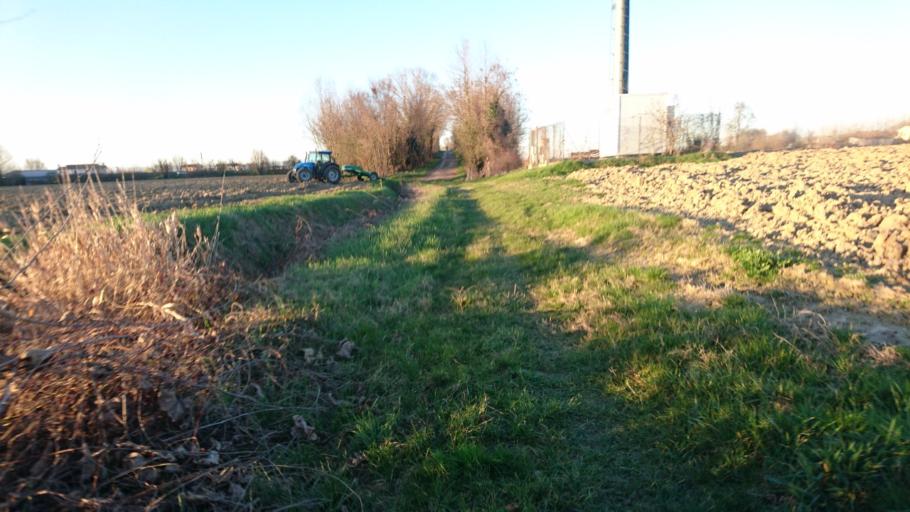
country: IT
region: Veneto
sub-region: Provincia di Padova
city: Albignasego
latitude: 45.3435
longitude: 11.9069
